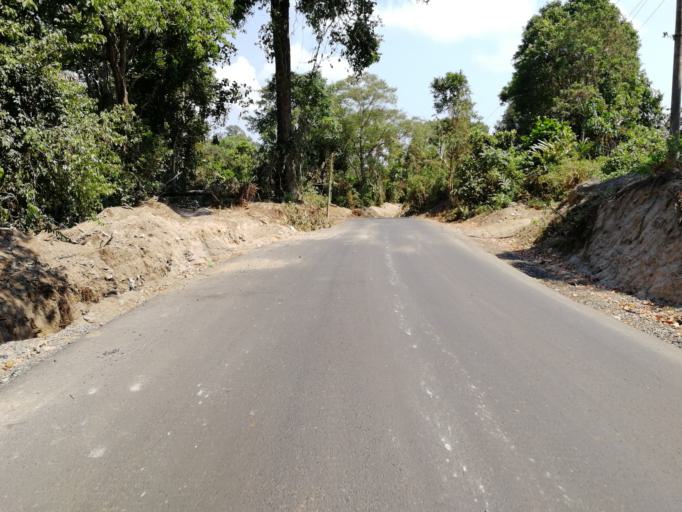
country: ID
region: West Nusa Tenggara
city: Lelongken
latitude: -8.3264
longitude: 116.4960
